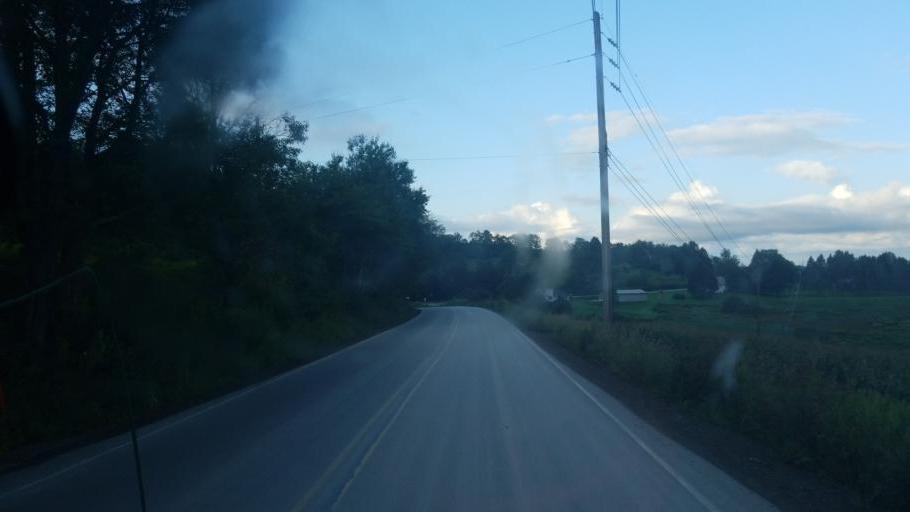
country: US
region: Pennsylvania
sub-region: Potter County
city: Galeton
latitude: 41.8511
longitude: -77.7714
